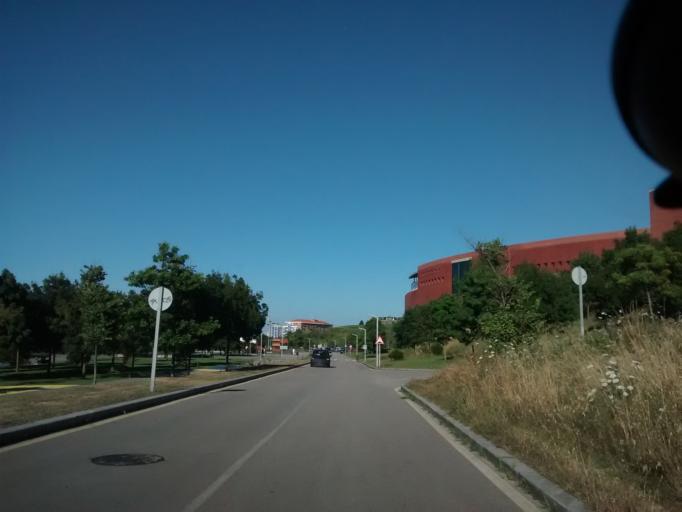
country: ES
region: Cantabria
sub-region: Provincia de Cantabria
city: Santander
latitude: 43.4726
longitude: -3.8017
